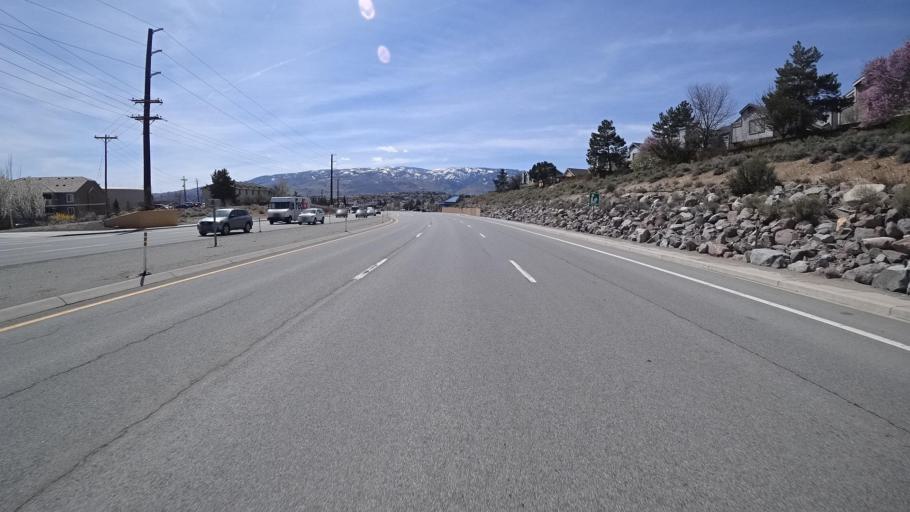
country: US
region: Nevada
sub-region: Washoe County
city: Reno
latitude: 39.5385
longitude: -119.8638
